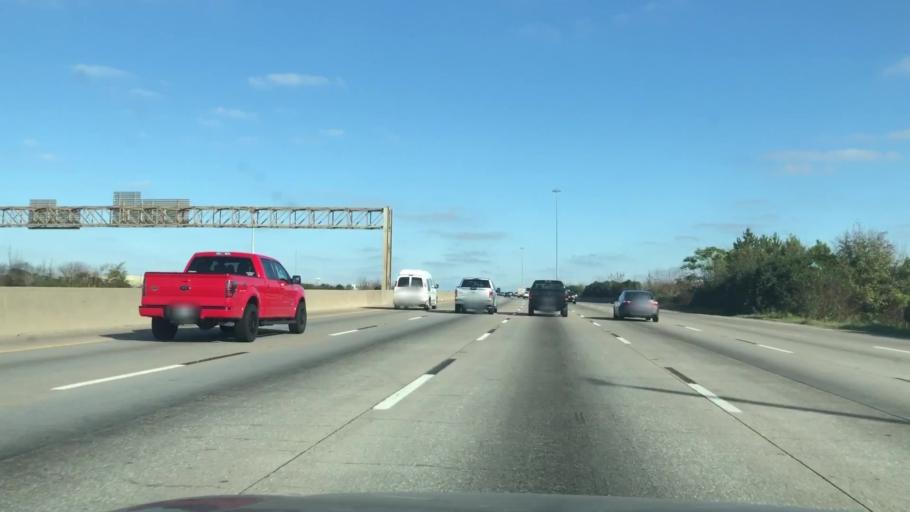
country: US
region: Texas
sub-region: Harris County
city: Galena Park
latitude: 29.7414
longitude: -95.2649
